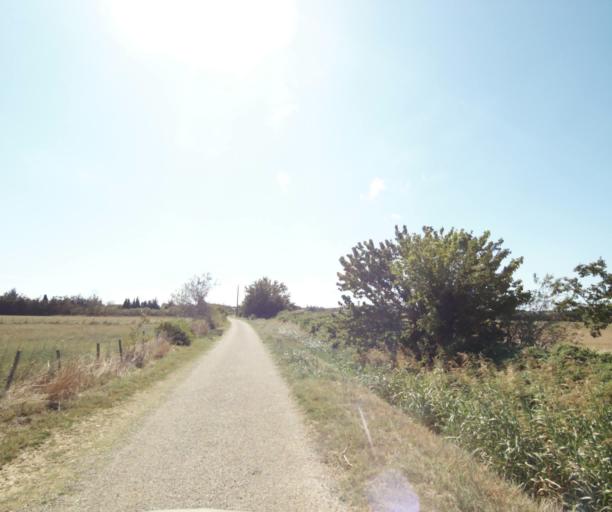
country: FR
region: Languedoc-Roussillon
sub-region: Departement du Gard
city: Bouillargues
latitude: 43.8096
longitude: 4.4240
